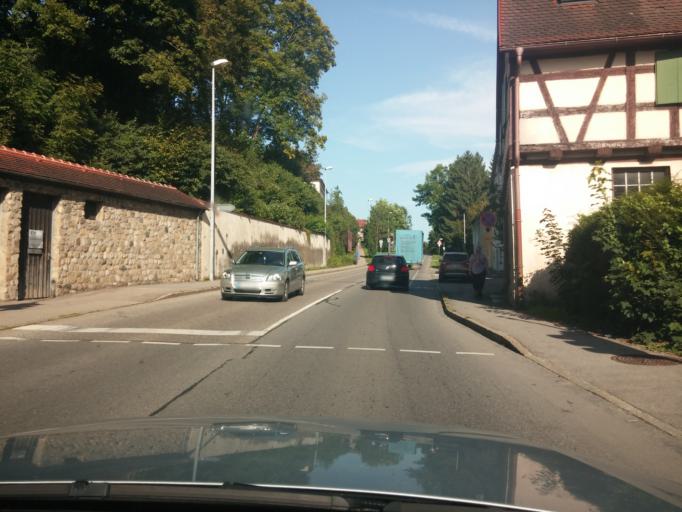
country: DE
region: Baden-Wuerttemberg
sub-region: Tuebingen Region
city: Leutkirch im Allgau
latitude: 47.8242
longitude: 10.0267
